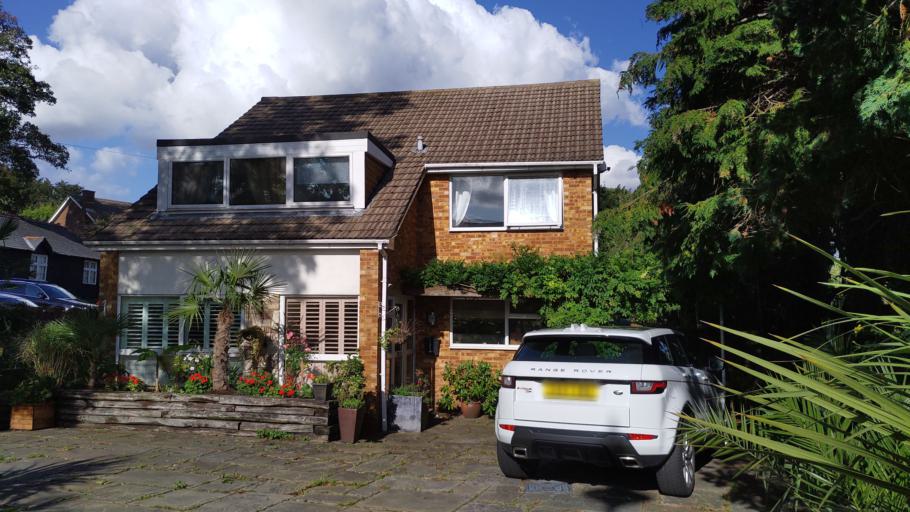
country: GB
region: England
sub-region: Hertfordshire
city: Potters Bar
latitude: 51.7041
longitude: -0.1494
